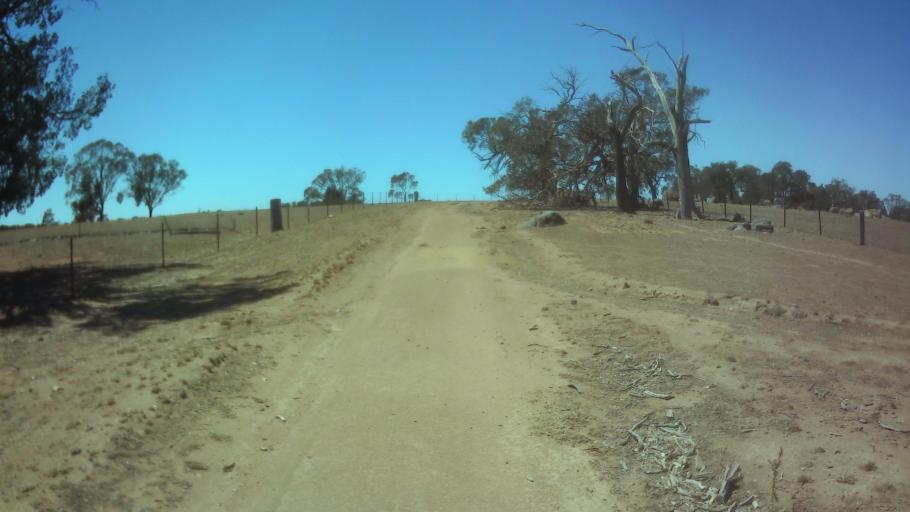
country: AU
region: New South Wales
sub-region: Cowra
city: Cowra
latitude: -33.8997
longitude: 148.5081
